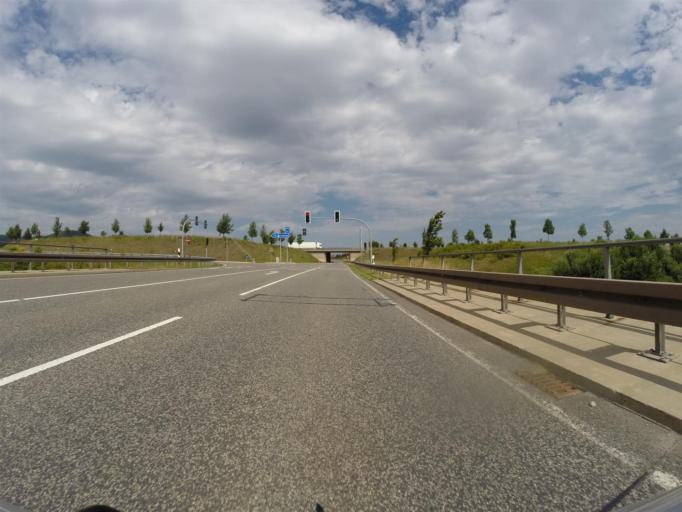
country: DE
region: Thuringia
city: Niedergebra
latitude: 51.4315
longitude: 10.6000
